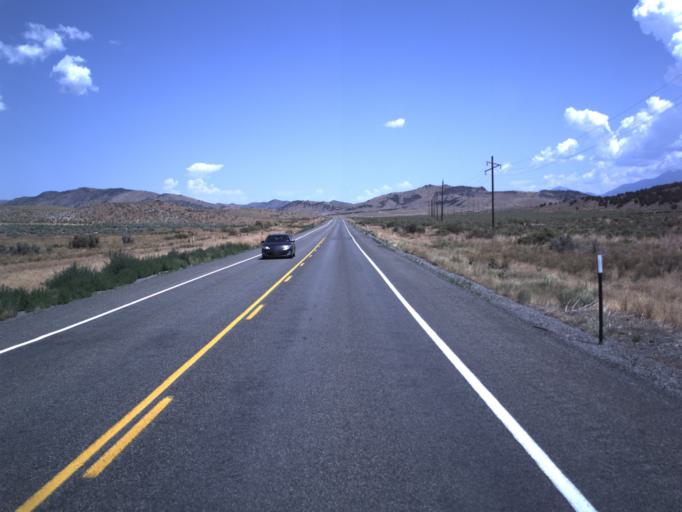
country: US
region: Utah
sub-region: Juab County
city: Nephi
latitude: 39.6112
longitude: -112.1340
